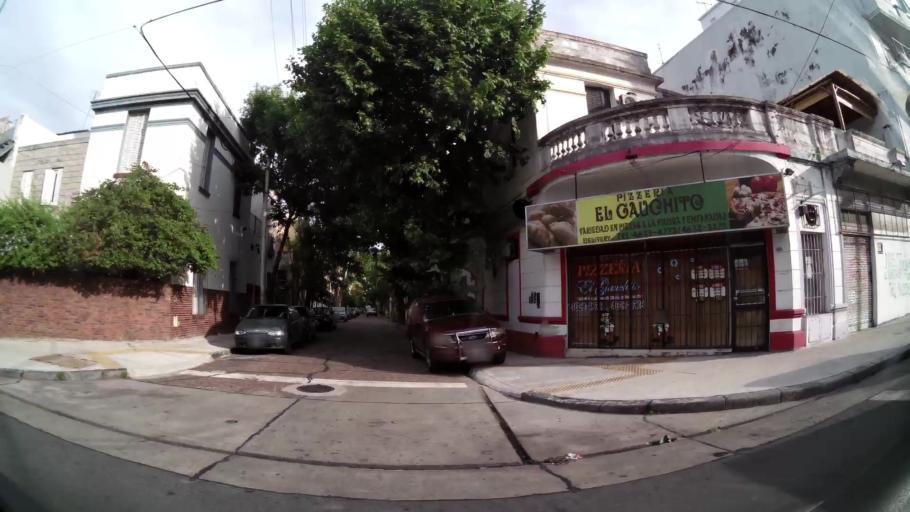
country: AR
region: Buenos Aires F.D.
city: Villa Santa Rita
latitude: -34.6409
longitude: -58.4563
